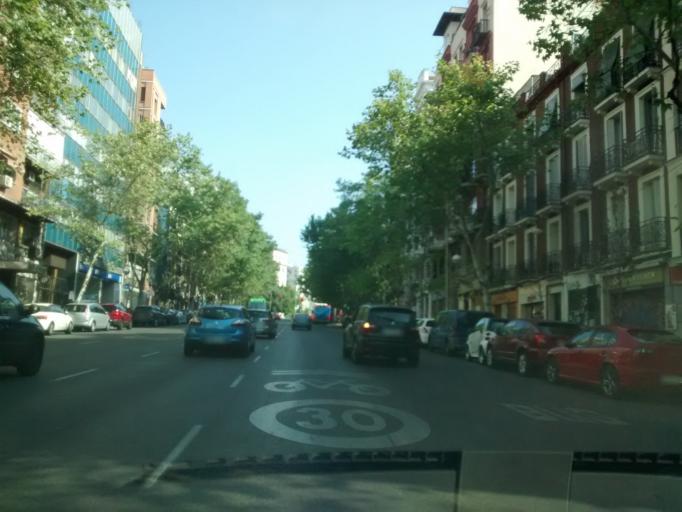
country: ES
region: Madrid
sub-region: Provincia de Madrid
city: Arganzuela
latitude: 40.4053
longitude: -3.6934
